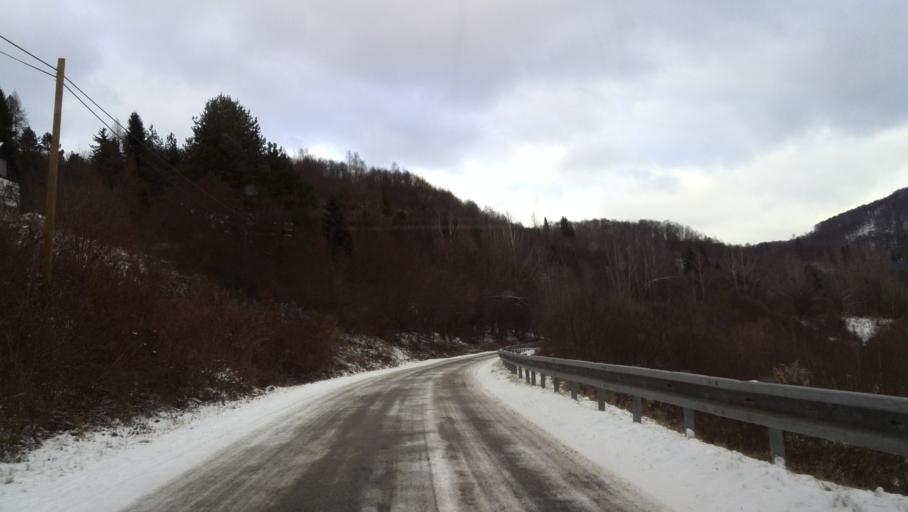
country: SK
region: Kosicky
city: Gelnica
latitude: 48.8253
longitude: 21.0655
